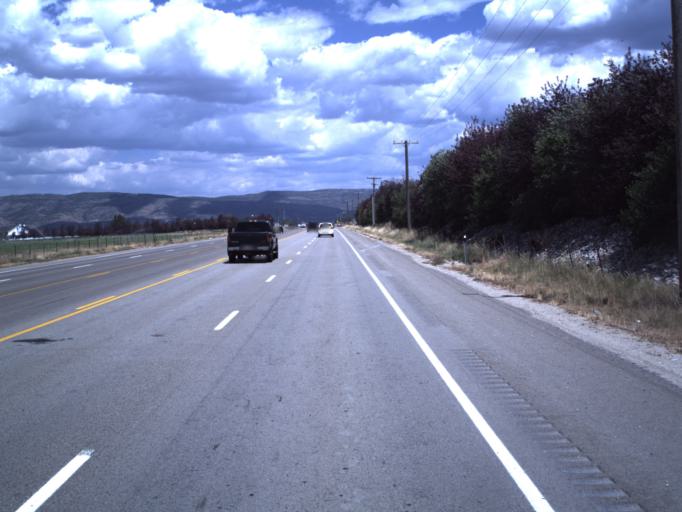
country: US
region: Utah
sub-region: Wasatch County
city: Midway
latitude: 40.4663
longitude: -111.4556
